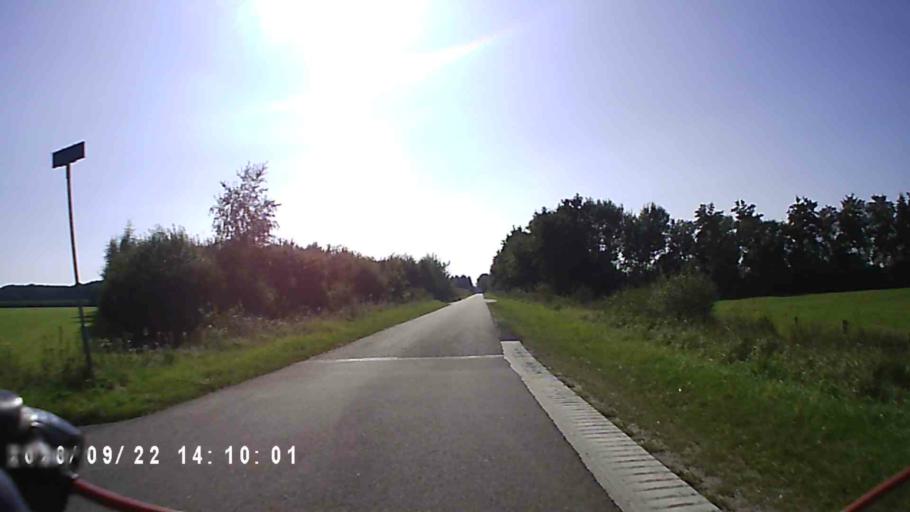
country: NL
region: Groningen
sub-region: Gemeente Leek
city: Leek
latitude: 53.0854
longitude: 6.4237
